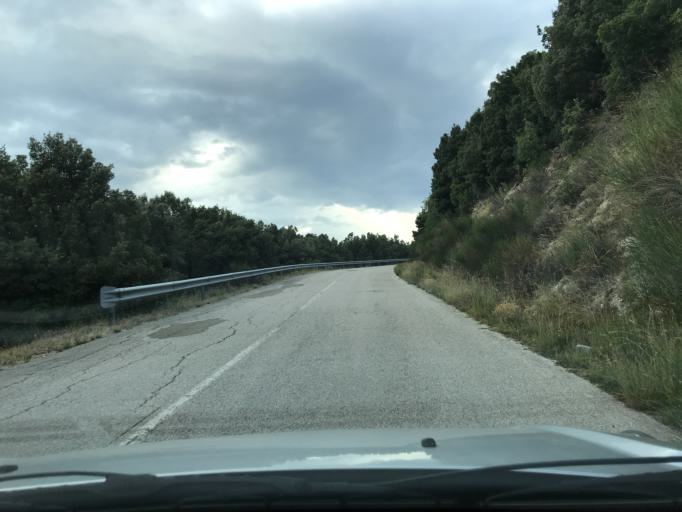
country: IT
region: Umbria
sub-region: Provincia di Terni
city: Montecchio
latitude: 42.6882
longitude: 12.2964
